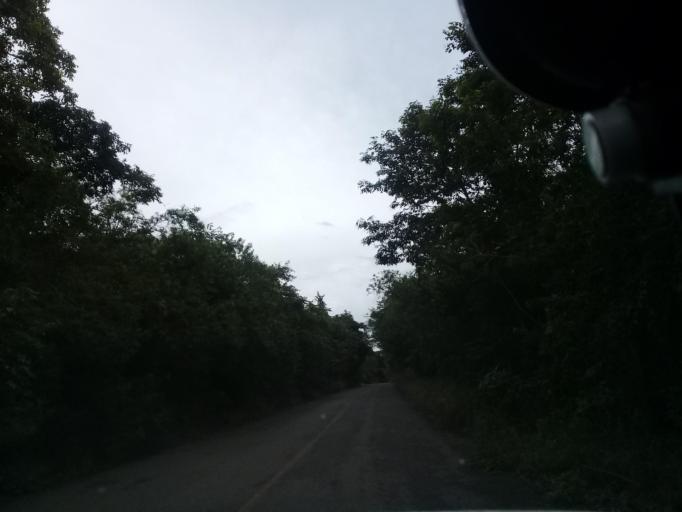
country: MX
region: Hidalgo
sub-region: Huejutla de Reyes
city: Chalahuiyapa
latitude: 21.2007
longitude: -98.3456
